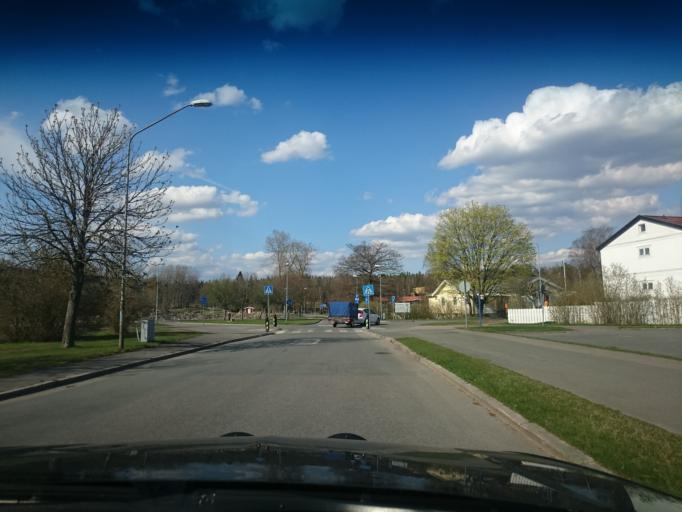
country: SE
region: Joenkoeping
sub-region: Vetlanda Kommun
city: Vetlanda
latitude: 57.4324
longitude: 15.0854
